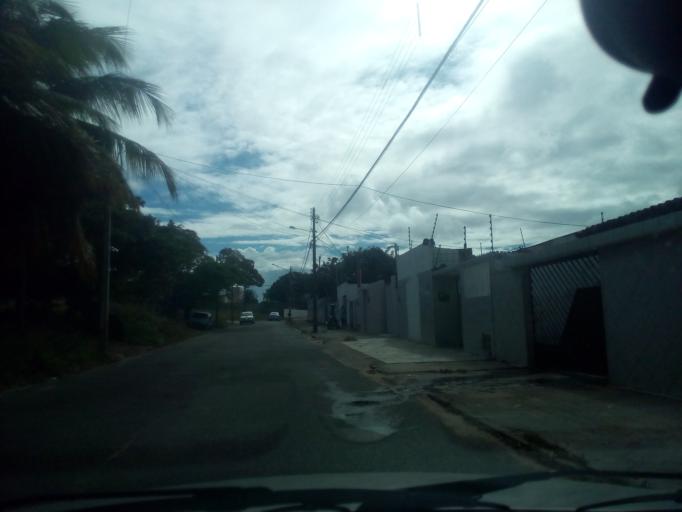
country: BR
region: Rio Grande do Norte
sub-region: Parnamirim
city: Parnamirim
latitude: -5.8713
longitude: -35.2009
